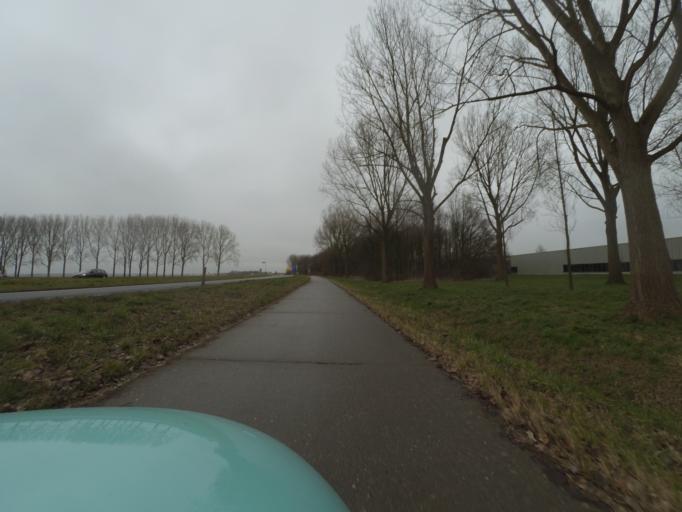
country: NL
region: Flevoland
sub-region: Gemeente Dronten
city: Dronten
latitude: 52.5381
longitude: 5.7310
